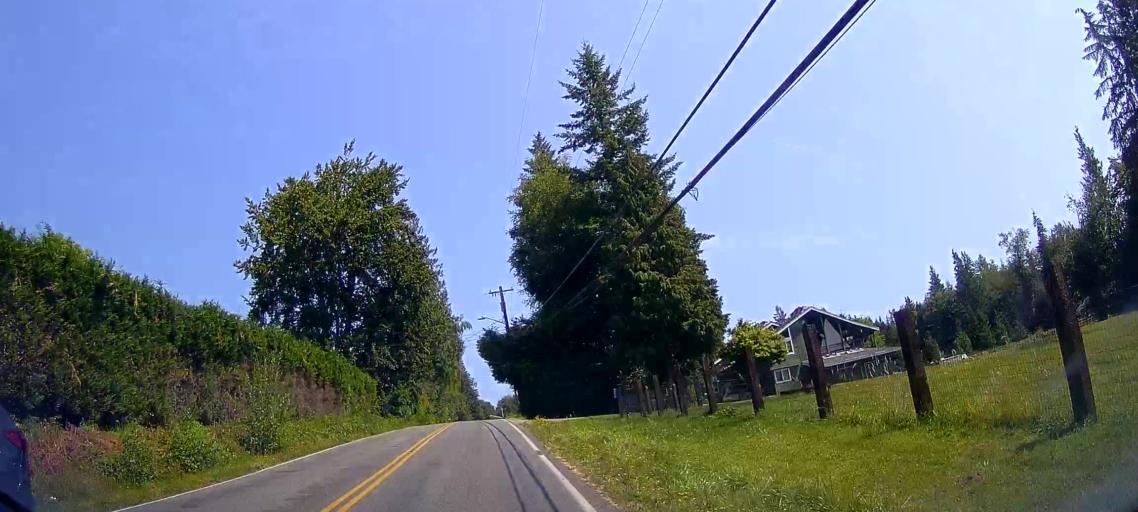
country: US
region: Washington
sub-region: Snohomish County
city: Sisco Heights
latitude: 48.0919
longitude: -122.1245
